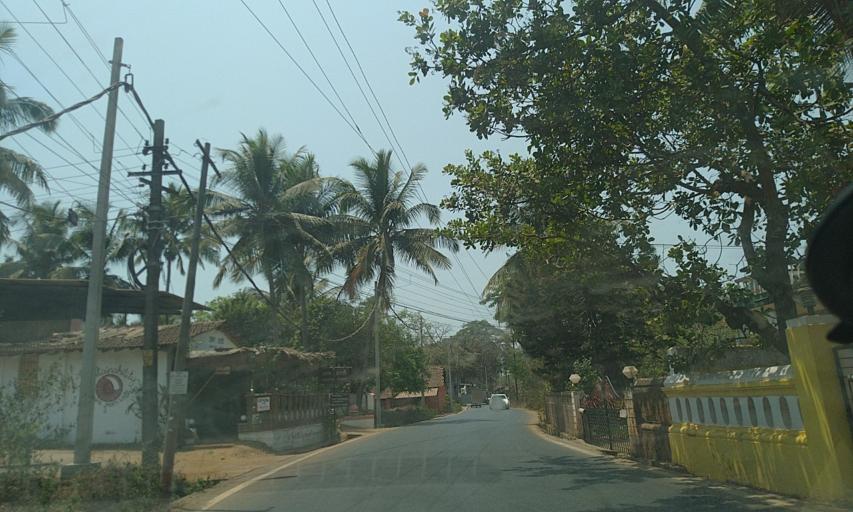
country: IN
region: Goa
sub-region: North Goa
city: Solim
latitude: 15.5905
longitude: 73.7693
